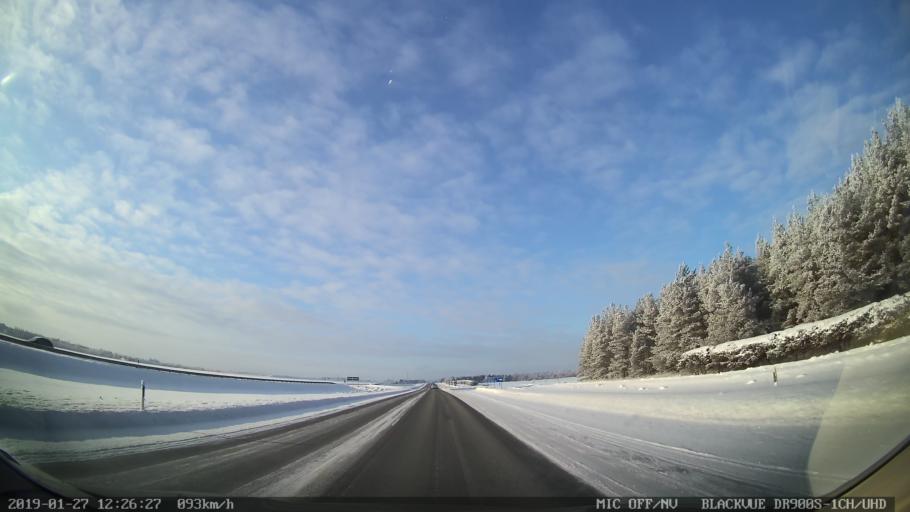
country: EE
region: Harju
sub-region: Maardu linn
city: Maardu
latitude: 59.4506
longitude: 25.0692
